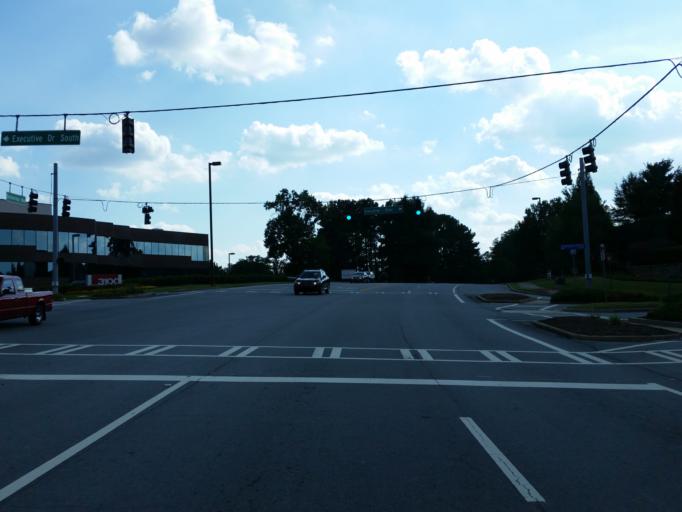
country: US
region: Georgia
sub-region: Gwinnett County
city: Duluth
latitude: 33.9556
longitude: -84.1128
